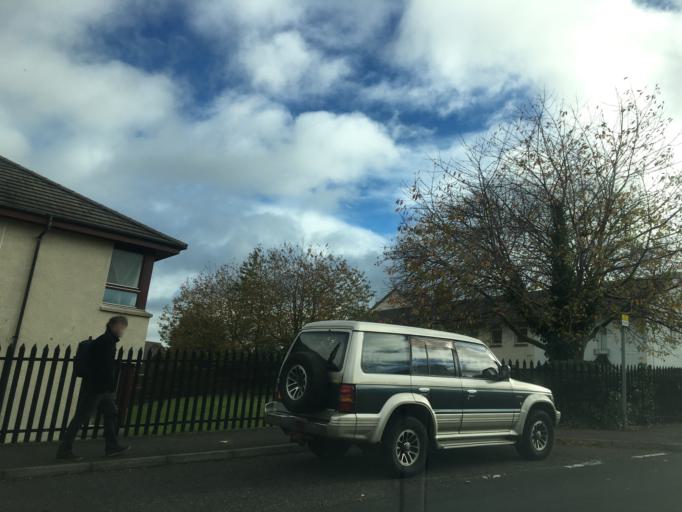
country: GB
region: Scotland
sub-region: Midlothian
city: Loanhead
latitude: 55.9209
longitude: -3.1546
